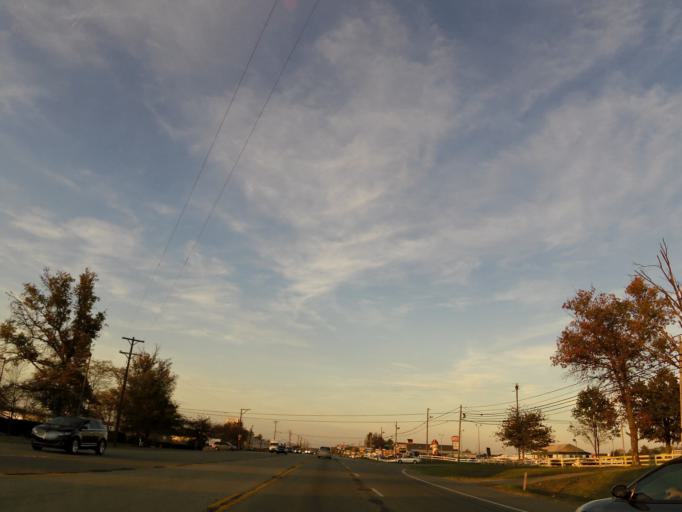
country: US
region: Kentucky
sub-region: Jessamine County
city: Nicholasville
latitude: 37.9099
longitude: -84.5602
